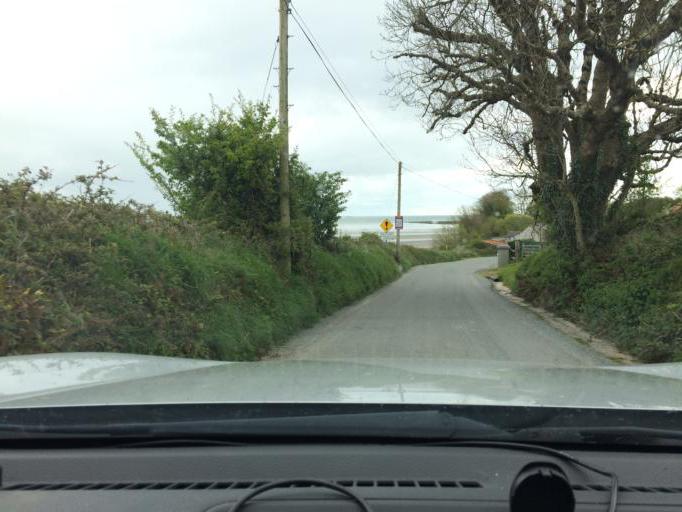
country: IE
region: Munster
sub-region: Waterford
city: Dungarvan
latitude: 52.0585
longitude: -7.6031
